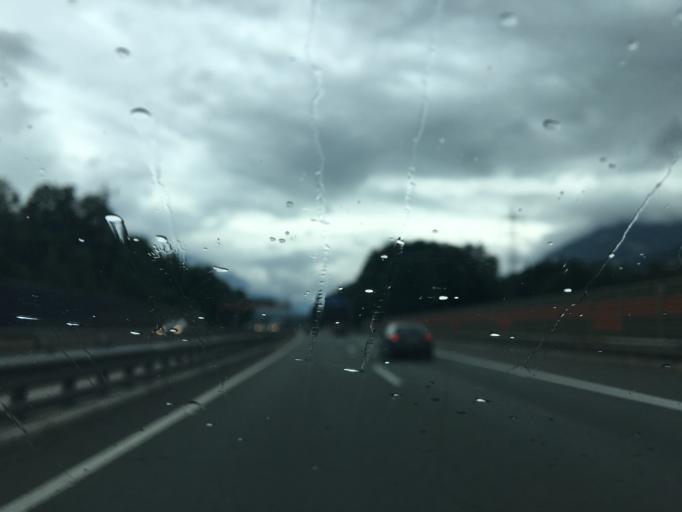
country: AT
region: Tyrol
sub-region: Politischer Bezirk Schwaz
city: Vomp
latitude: 47.3266
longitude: 11.6739
